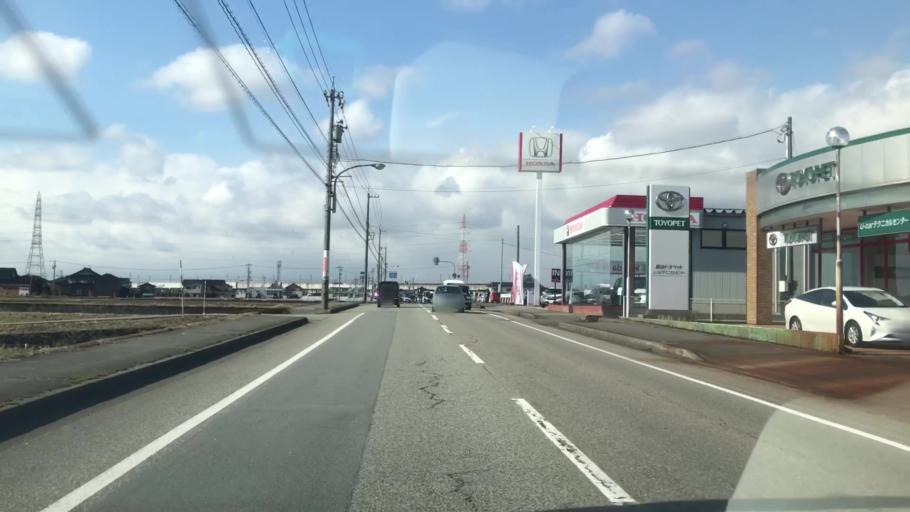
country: JP
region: Toyama
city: Nishishinminato
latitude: 36.7197
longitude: 137.0772
